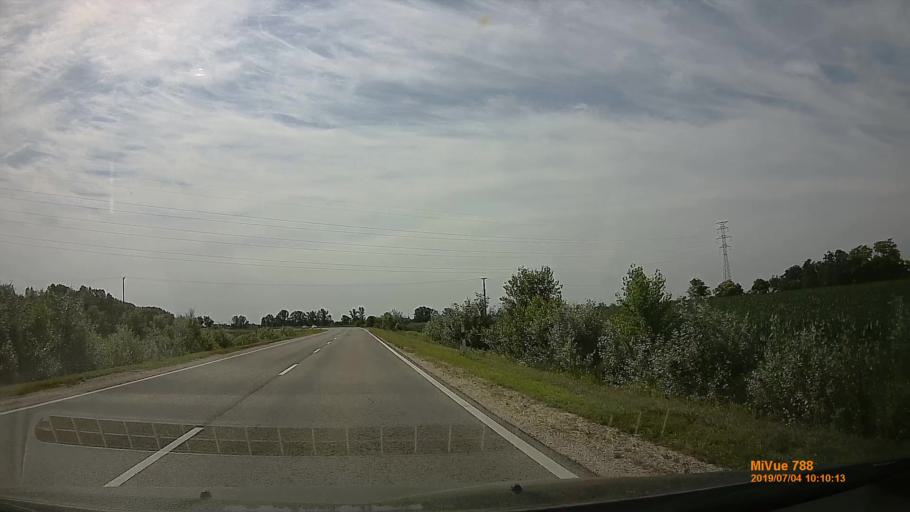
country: HU
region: Komarom-Esztergom
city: Komarom
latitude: 47.7225
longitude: 18.1089
